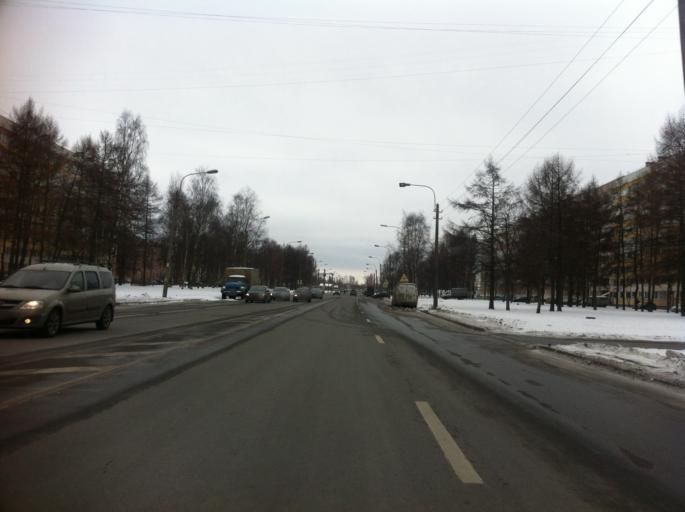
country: RU
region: St.-Petersburg
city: Uritsk
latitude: 59.8287
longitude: 30.1757
